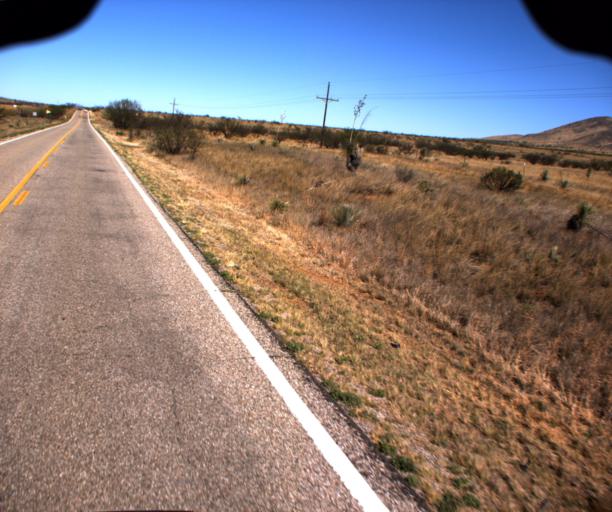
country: US
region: Arizona
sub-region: Cochise County
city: Huachuca City
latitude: 31.7101
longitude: -110.4493
